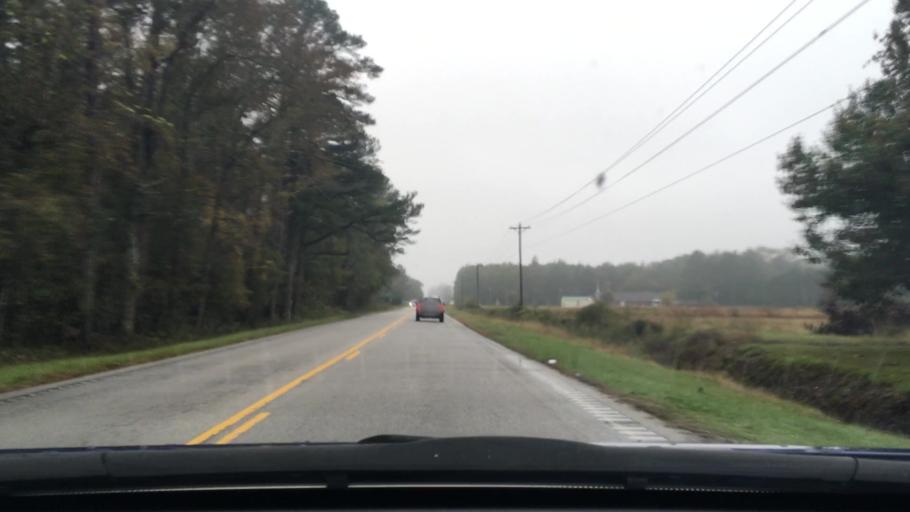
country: US
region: South Carolina
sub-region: Florence County
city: Timmonsville
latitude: 34.2257
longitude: -79.9976
